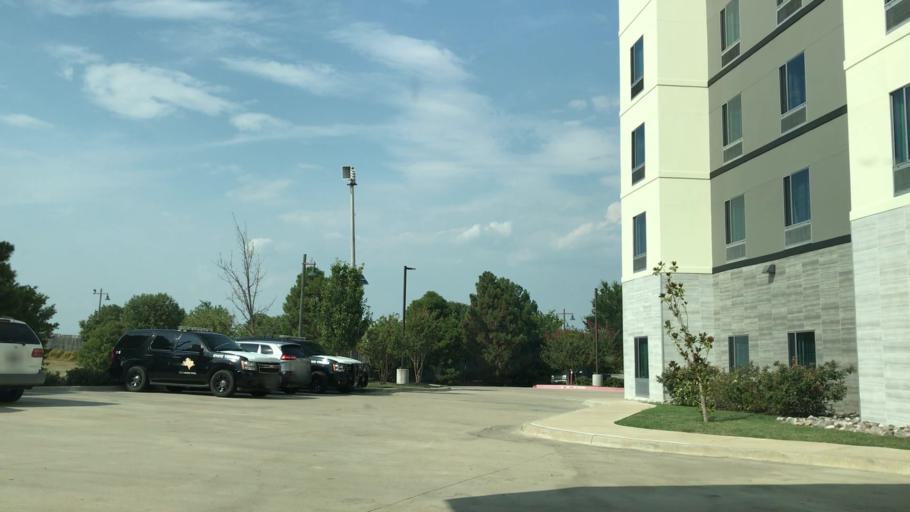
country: US
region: Texas
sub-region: Dallas County
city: Rowlett
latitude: 32.8644
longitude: -96.5410
